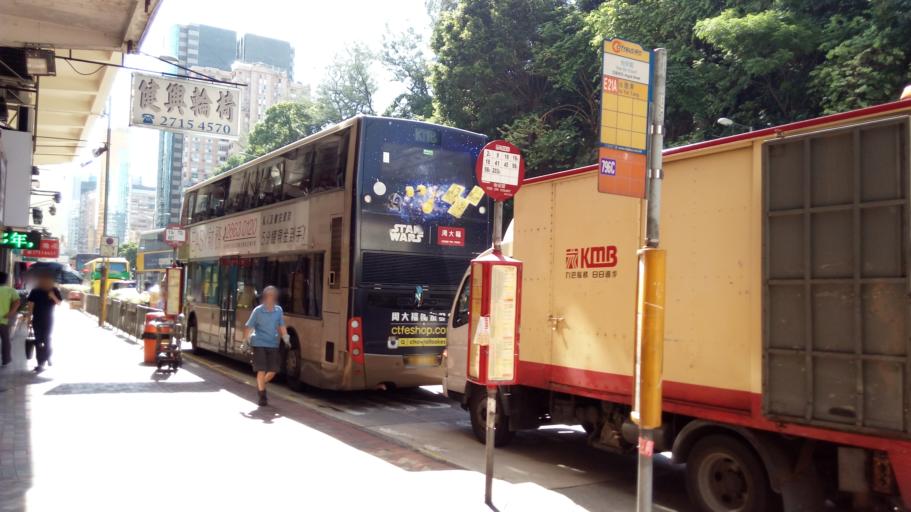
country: HK
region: Kowloon City
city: Kowloon
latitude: 22.3203
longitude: 114.1757
